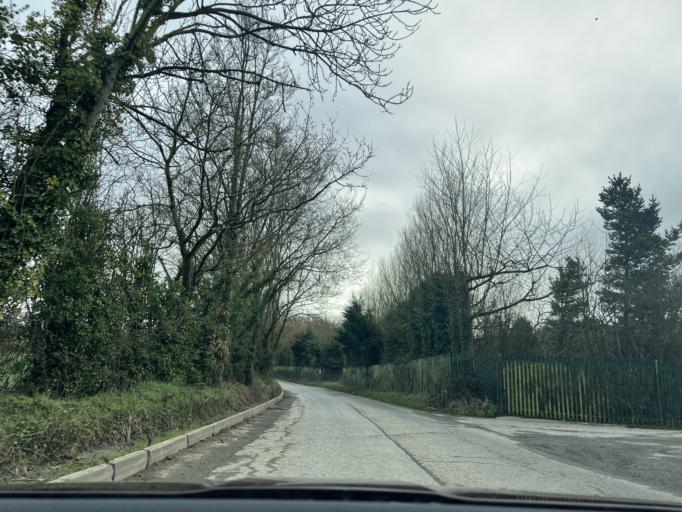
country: IE
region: Leinster
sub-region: Loch Garman
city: Castlebridge
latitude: 52.3835
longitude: -6.5633
